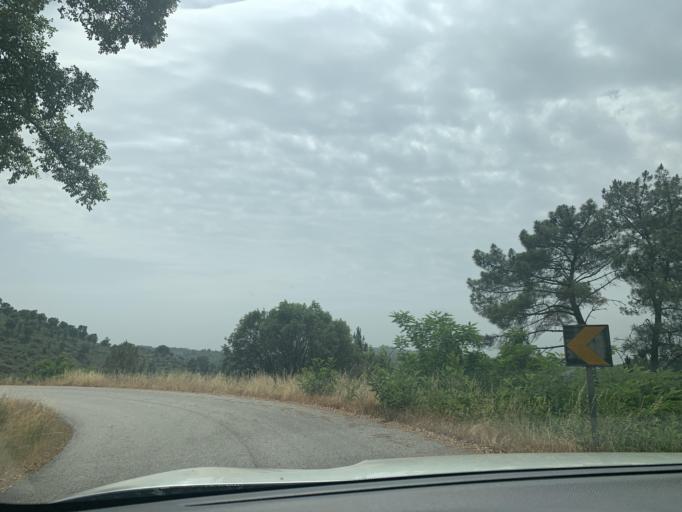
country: PT
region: Guarda
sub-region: Fornos de Algodres
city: Fornos de Algodres
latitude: 40.5693
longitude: -7.5982
